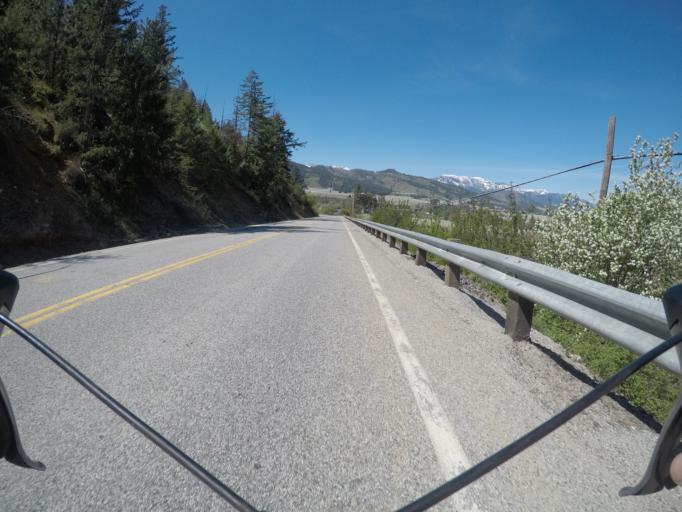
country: US
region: Washington
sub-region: Chelan County
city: Cashmere
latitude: 47.5301
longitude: -120.5302
